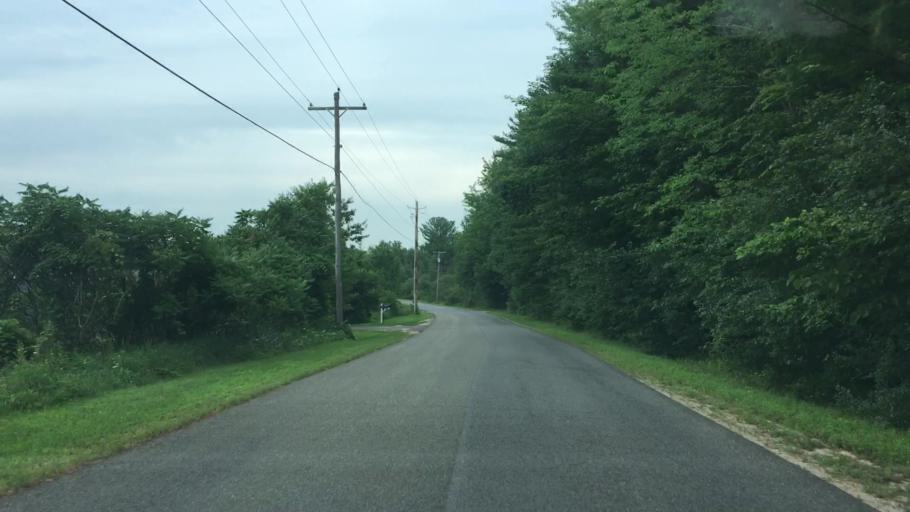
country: US
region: New York
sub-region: Clinton County
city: Peru
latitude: 44.6026
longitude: -73.6067
